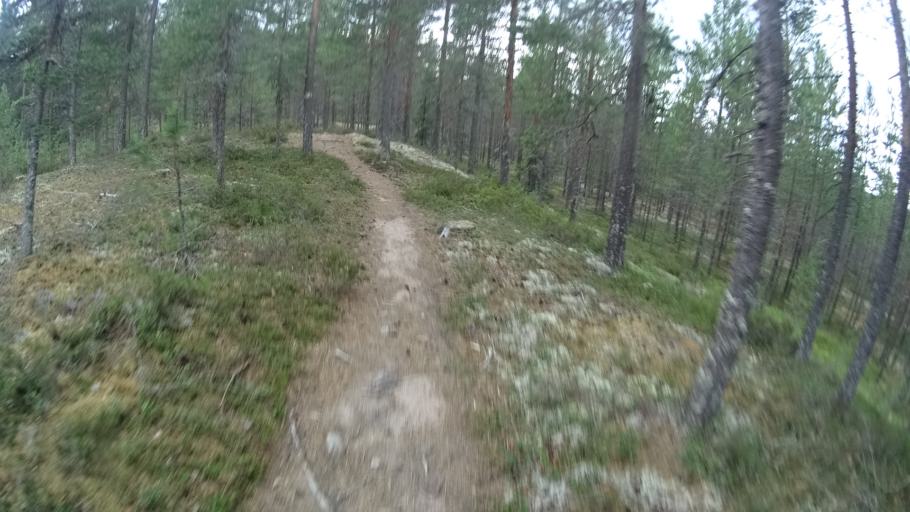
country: FI
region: Satakunta
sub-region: Pohjois-Satakunta
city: Jaemijaervi
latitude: 61.7708
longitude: 22.7886
